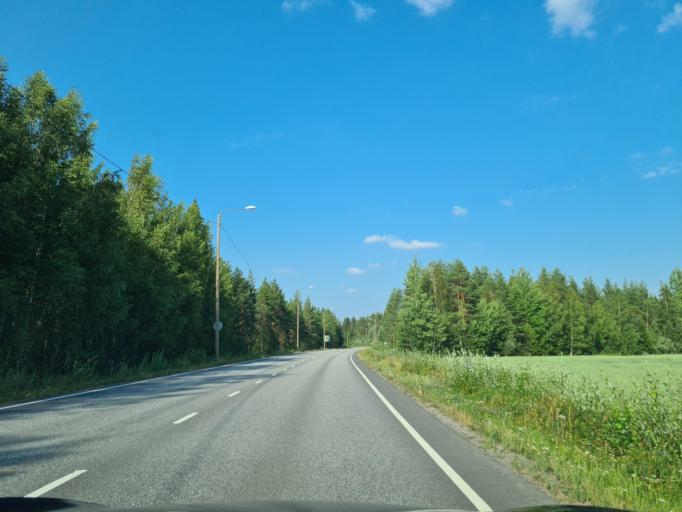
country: FI
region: Satakunta
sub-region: Pohjois-Satakunta
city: Karvia
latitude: 62.0797
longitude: 22.5181
